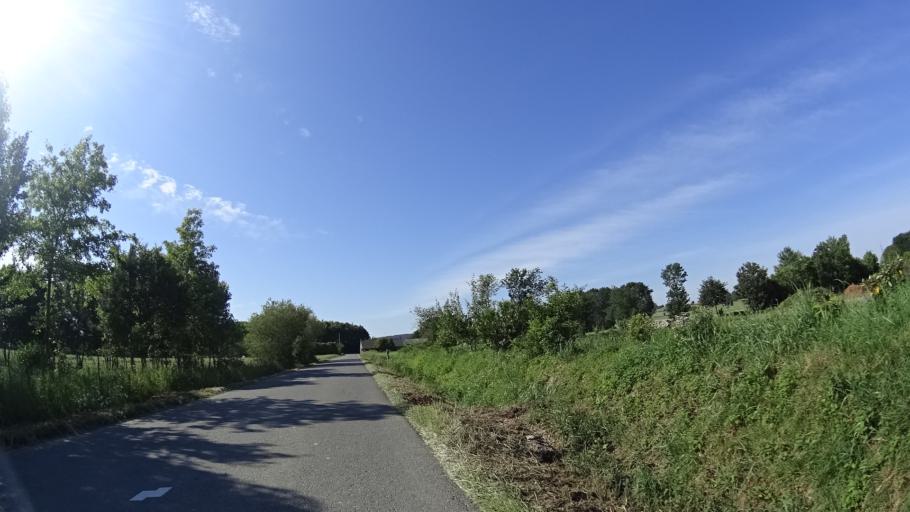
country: FR
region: Brittany
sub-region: Departement d'Ille-et-Vilaine
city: Guipry
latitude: 47.8039
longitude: -1.8491
